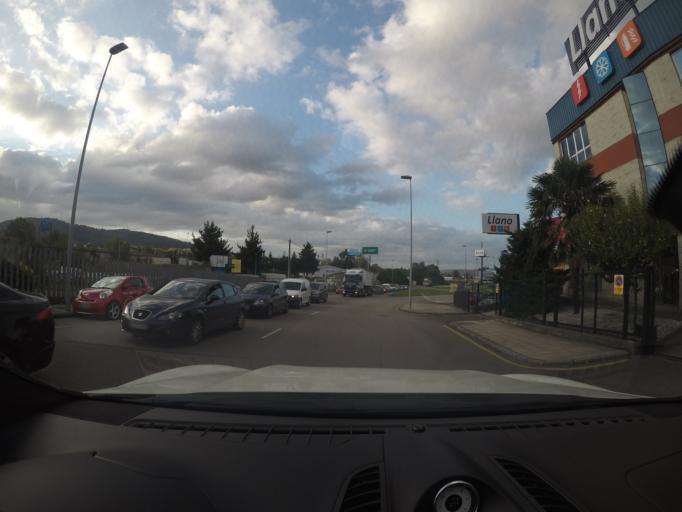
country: ES
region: Asturias
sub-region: Province of Asturias
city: Lugones
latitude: 43.3753
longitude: -5.8106
